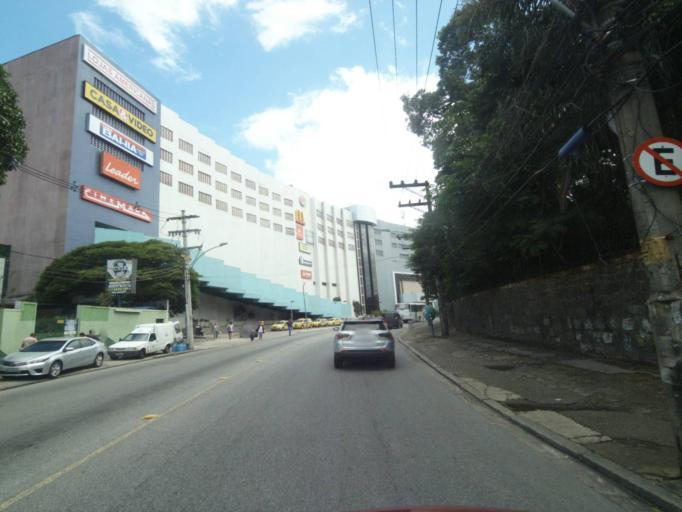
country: BR
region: Rio de Janeiro
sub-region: Sao Joao De Meriti
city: Sao Joao de Meriti
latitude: -22.9249
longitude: -43.3600
